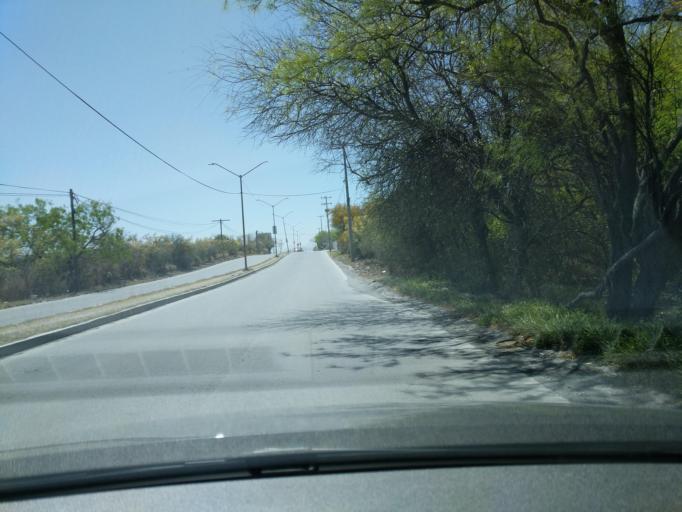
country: MX
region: Nuevo Leon
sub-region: Apodaca
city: Artemio Trevino
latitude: 25.8008
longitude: -100.1565
